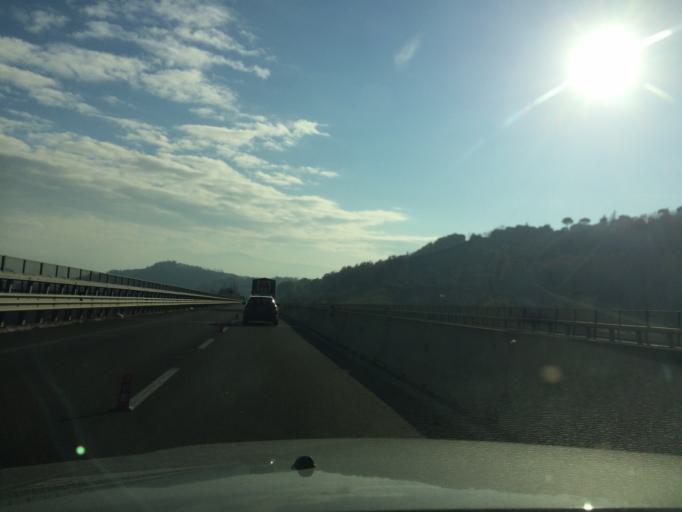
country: IT
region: Umbria
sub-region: Provincia di Terni
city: San Gemini
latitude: 42.6160
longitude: 12.5542
